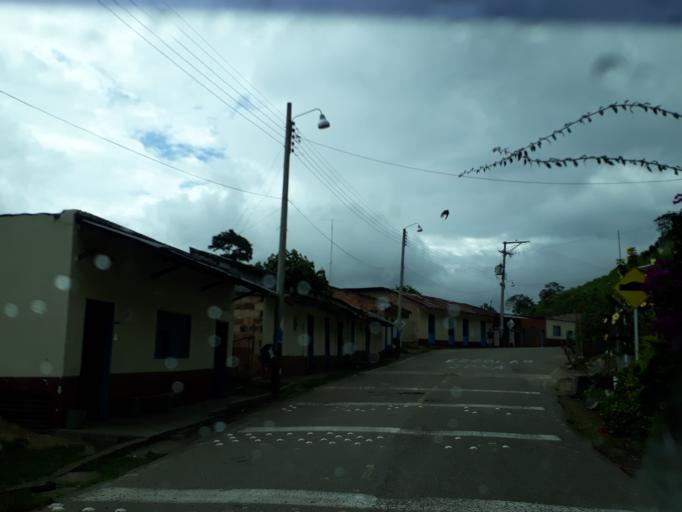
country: CO
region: Cundinamarca
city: Cabrera
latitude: 4.0253
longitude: -74.5133
